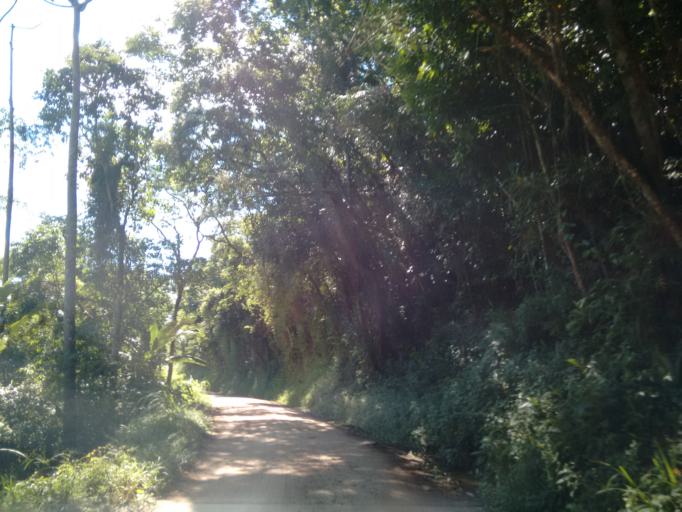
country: BR
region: Santa Catarina
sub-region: Indaial
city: Indaial
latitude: -26.9322
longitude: -49.1835
